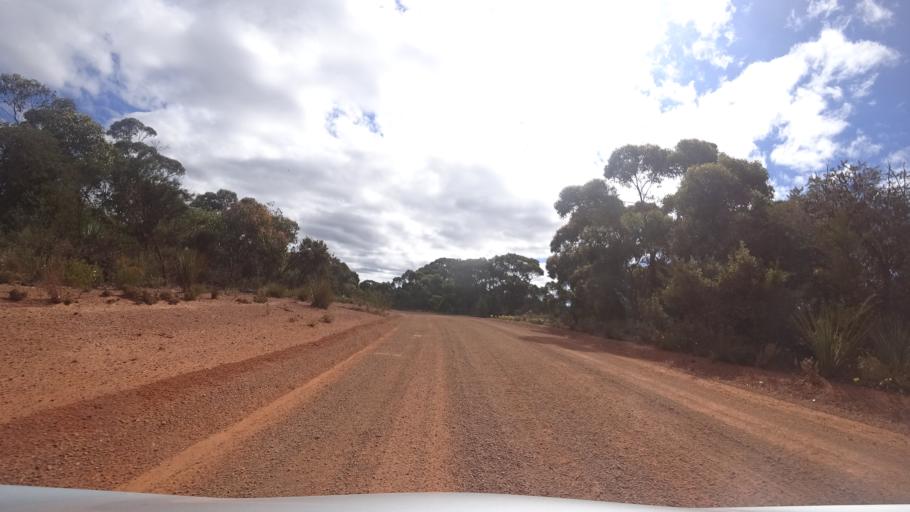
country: AU
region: South Australia
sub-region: Kangaroo Island
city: Kingscote
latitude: -35.7546
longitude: 136.9804
